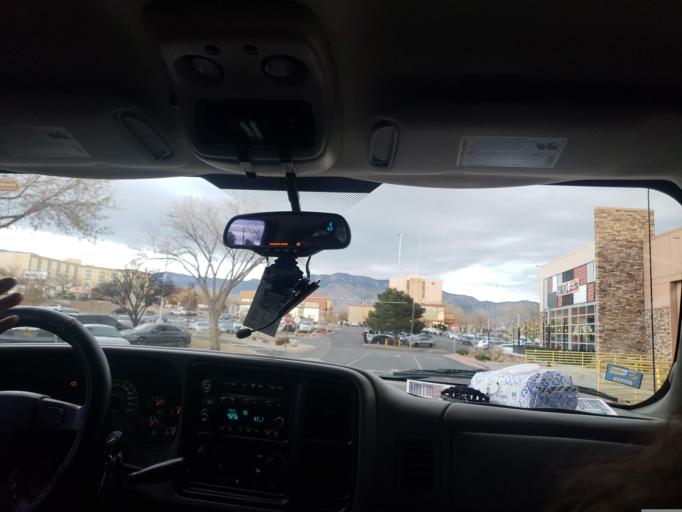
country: US
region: New Mexico
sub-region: Bernalillo County
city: Albuquerque
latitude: 35.1085
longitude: -106.5722
